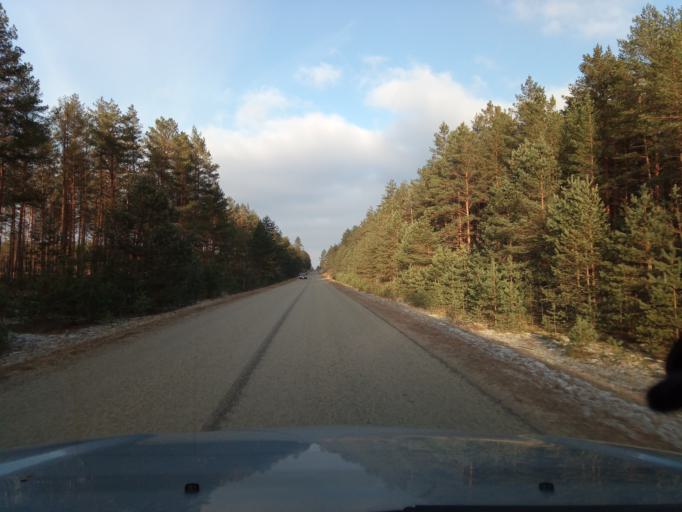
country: LT
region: Alytaus apskritis
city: Varena
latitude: 54.1706
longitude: 24.5085
